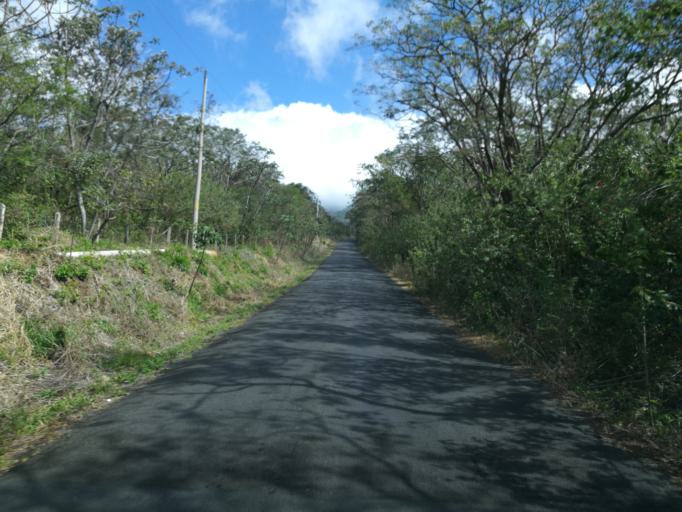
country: CR
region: Guanacaste
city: Liberia
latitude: 10.7656
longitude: -85.3525
